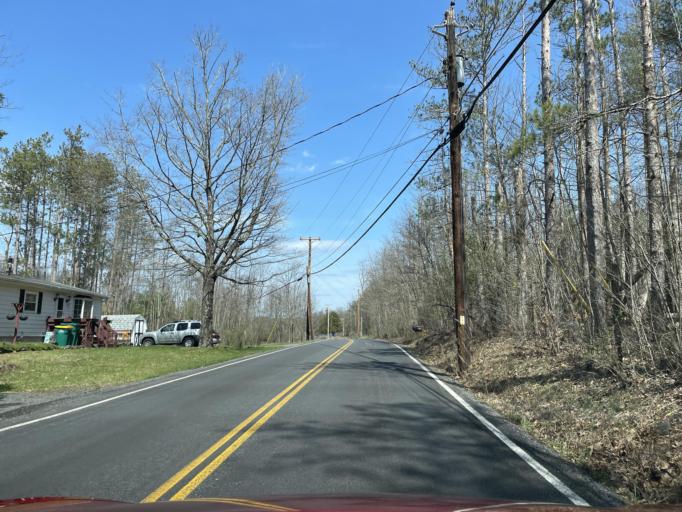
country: US
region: New York
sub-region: Ulster County
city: Manorville
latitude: 42.1145
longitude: -74.0183
